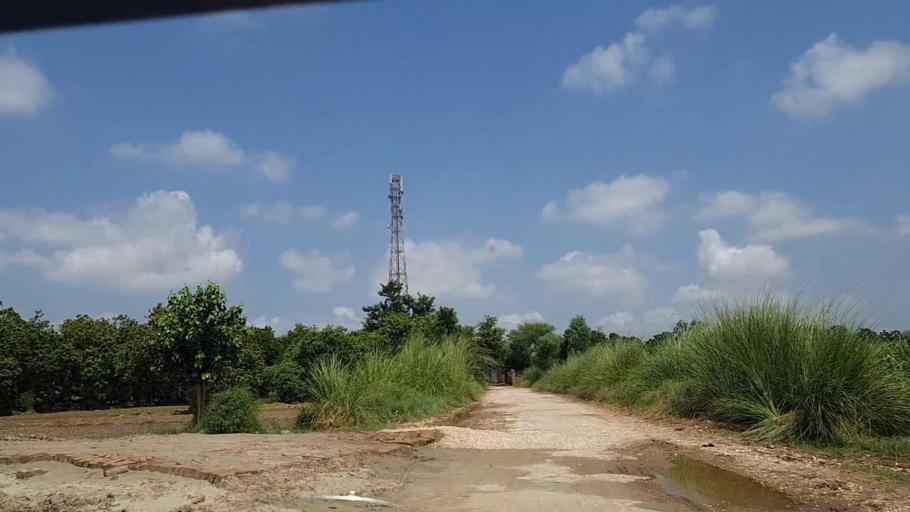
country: PK
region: Sindh
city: Tharu Shah
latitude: 26.9096
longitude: 68.0355
